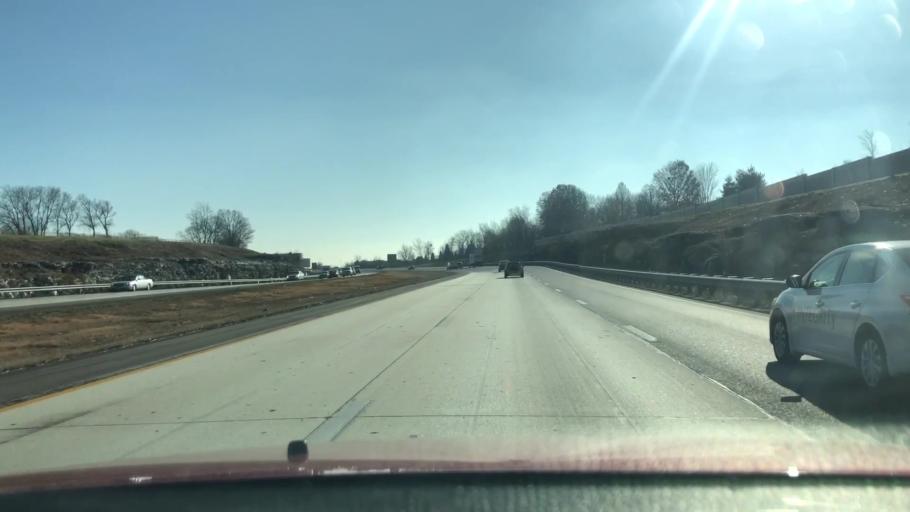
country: US
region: Missouri
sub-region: Greene County
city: Battlefield
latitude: 37.1363
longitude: -93.3079
